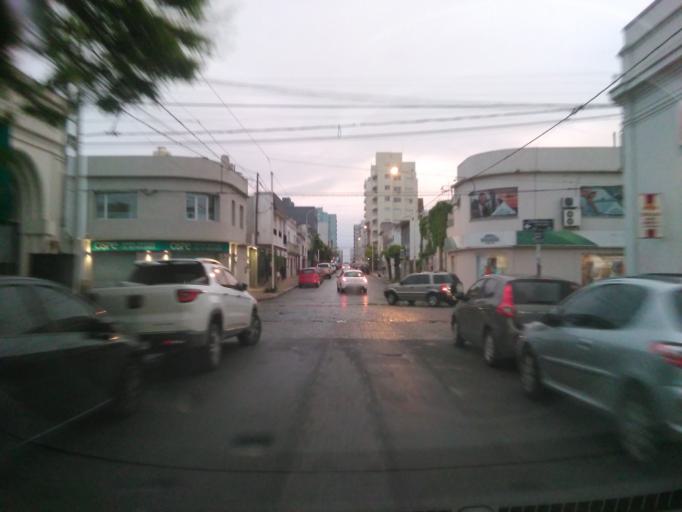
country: AR
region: Buenos Aires
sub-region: Partido de Tandil
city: Tandil
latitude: -37.3267
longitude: -59.1416
